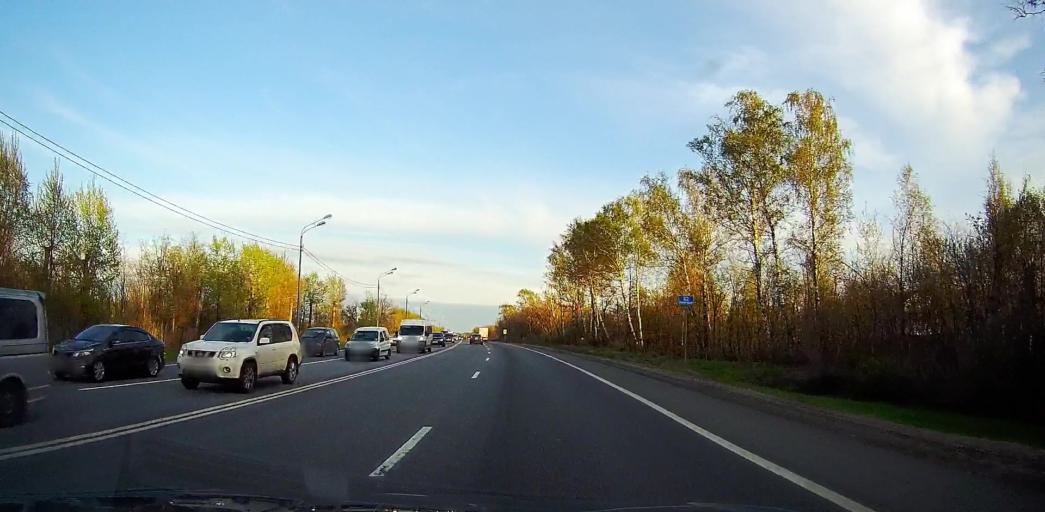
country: RU
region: Moskovskaya
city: Troitskoye
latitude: 55.2698
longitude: 38.5000
